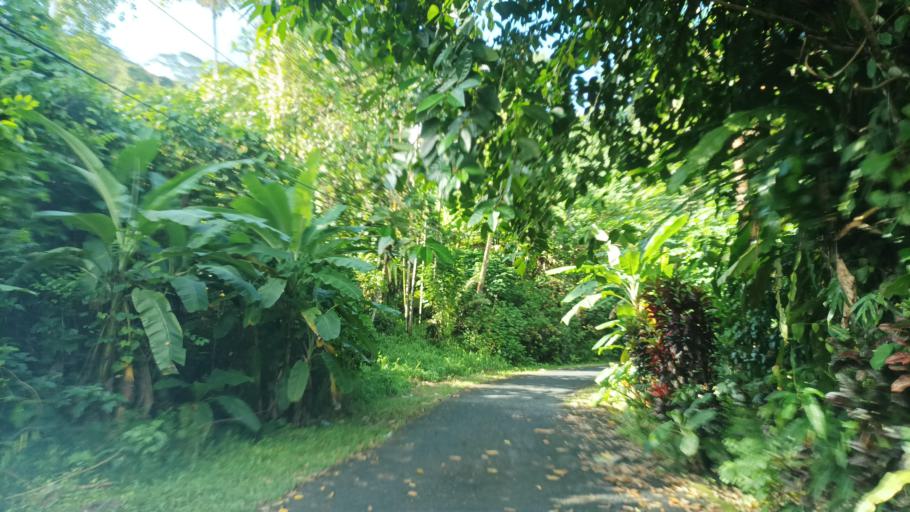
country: FM
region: Pohnpei
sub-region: Kolonia Municipality
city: Kolonia Town
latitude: 6.9597
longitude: 158.1951
